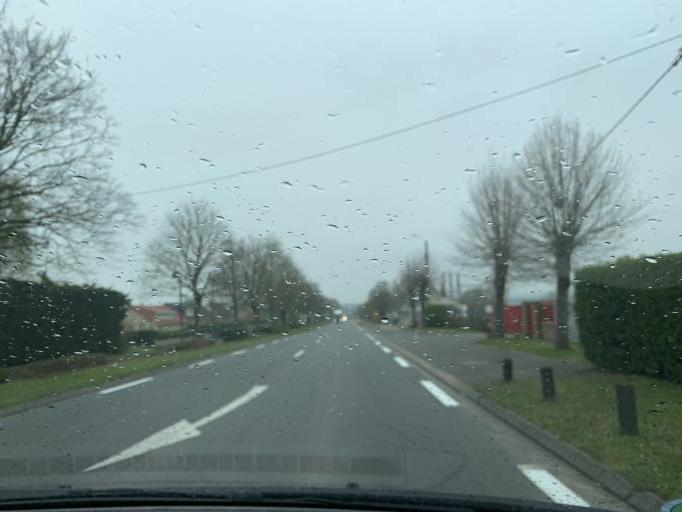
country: FR
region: Picardie
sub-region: Departement de la Somme
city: Nouvion
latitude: 50.2020
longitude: 1.7878
